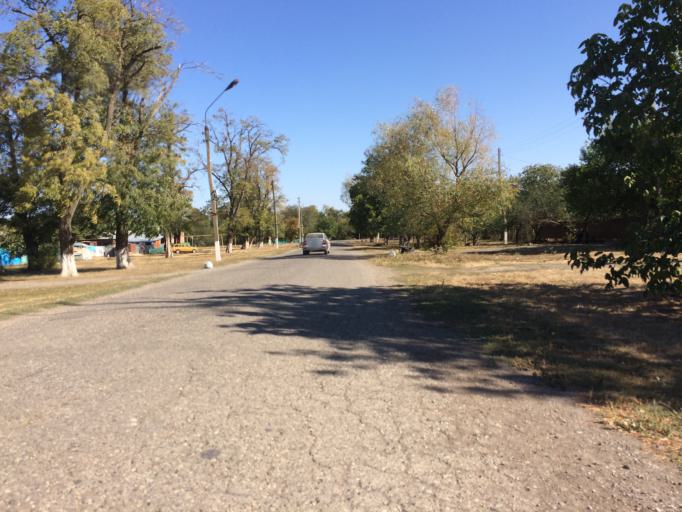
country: RU
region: Rostov
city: Gigant
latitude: 46.5191
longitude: 41.1897
